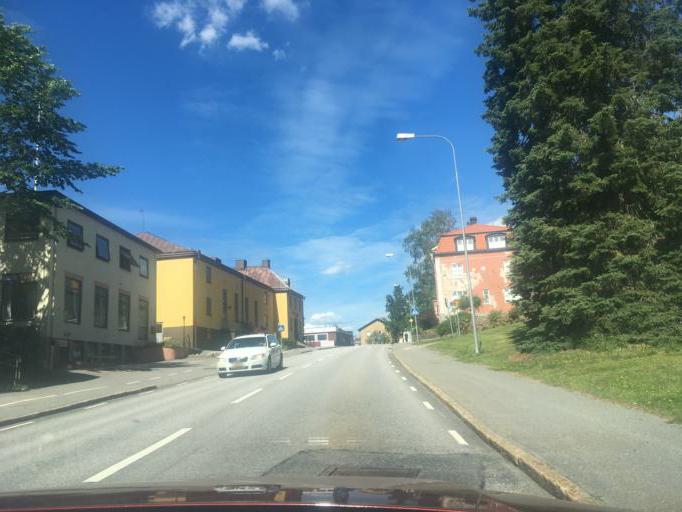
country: SE
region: OEstergoetland
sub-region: Valdemarsviks Kommun
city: Valdemarsvik
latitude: 58.2063
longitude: 16.5971
